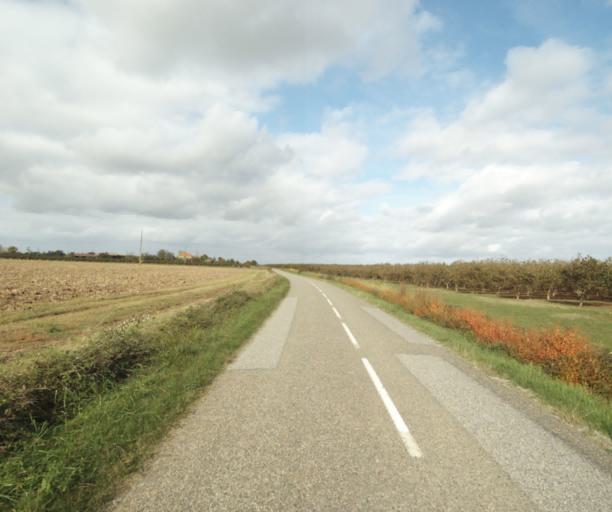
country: FR
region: Midi-Pyrenees
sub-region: Departement du Tarn-et-Garonne
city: Finhan
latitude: 43.9089
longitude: 1.1477
